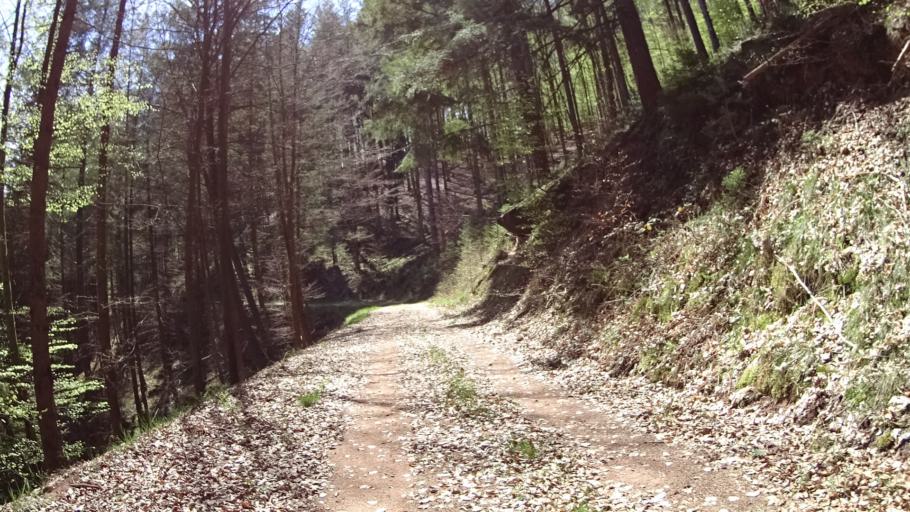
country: DE
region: Rheinland-Pfalz
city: Ramberg
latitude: 49.3093
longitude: 7.9941
